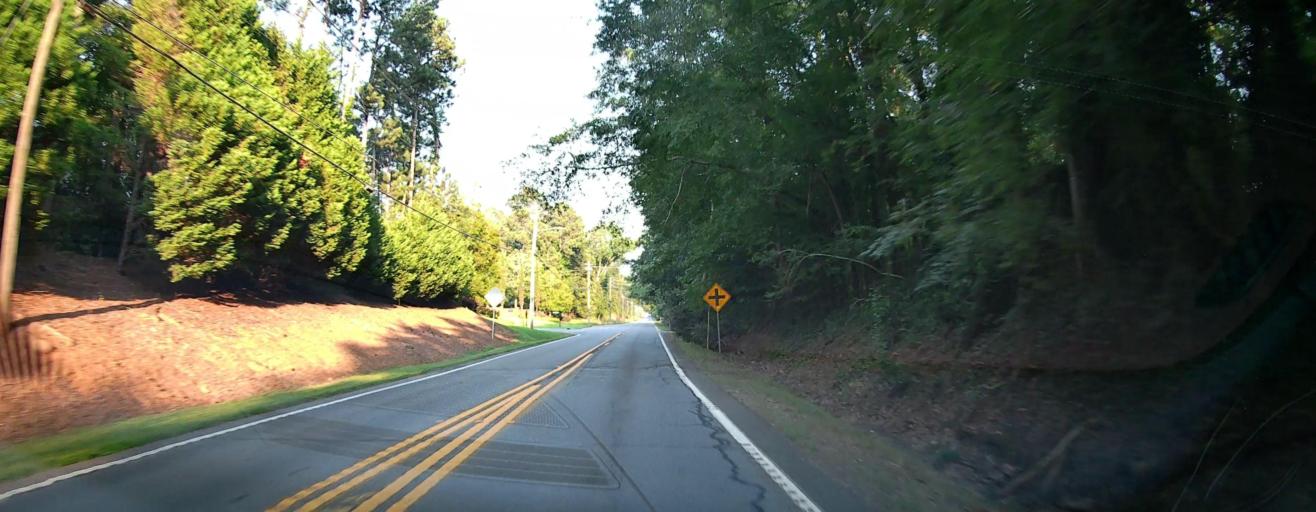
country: US
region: Georgia
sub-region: Bibb County
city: West Point
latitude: 32.8888
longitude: -83.7443
